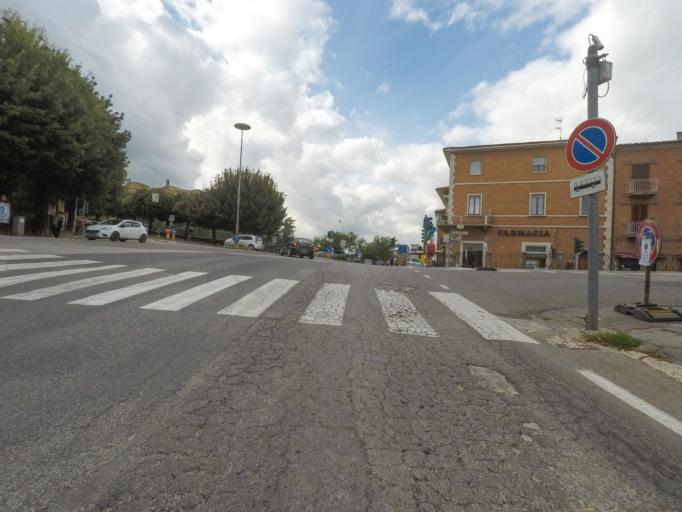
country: IT
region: Tuscany
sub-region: Provincia di Siena
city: Montepulciano
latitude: 43.0982
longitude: 11.7857
